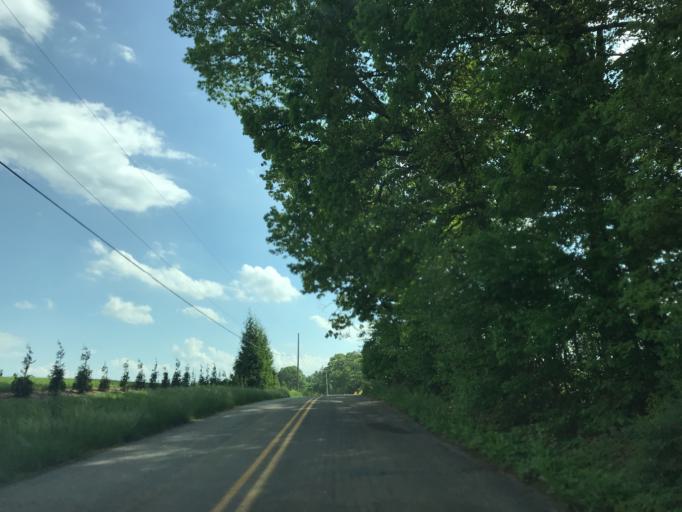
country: US
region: Pennsylvania
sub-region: York County
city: Susquehanna Trails
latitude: 39.6605
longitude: -76.3766
